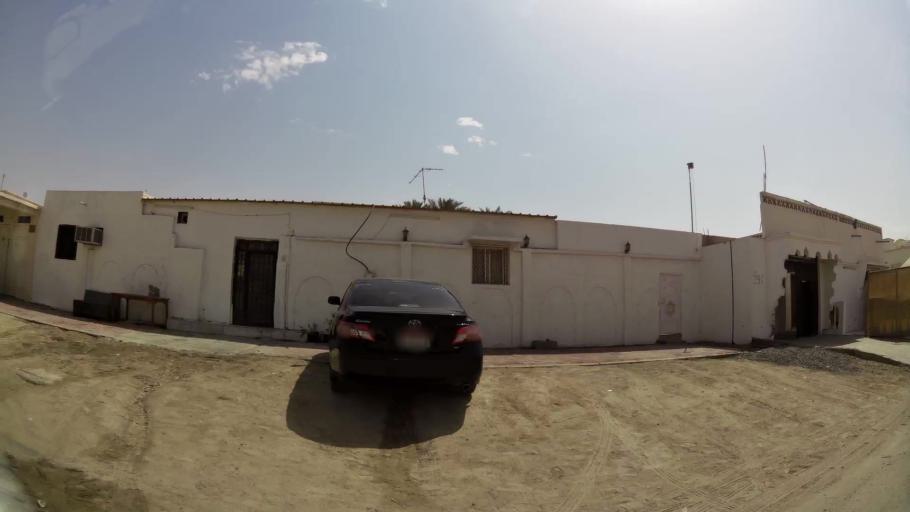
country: AE
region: Abu Dhabi
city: Abu Dhabi
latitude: 24.2956
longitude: 54.6434
